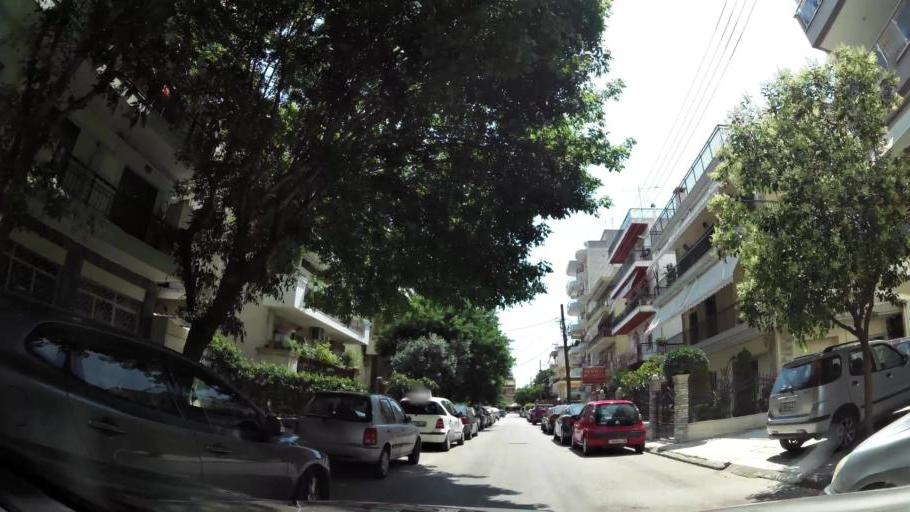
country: GR
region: Central Macedonia
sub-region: Nomos Thessalonikis
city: Ampelokipoi
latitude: 40.6583
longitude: 22.9294
